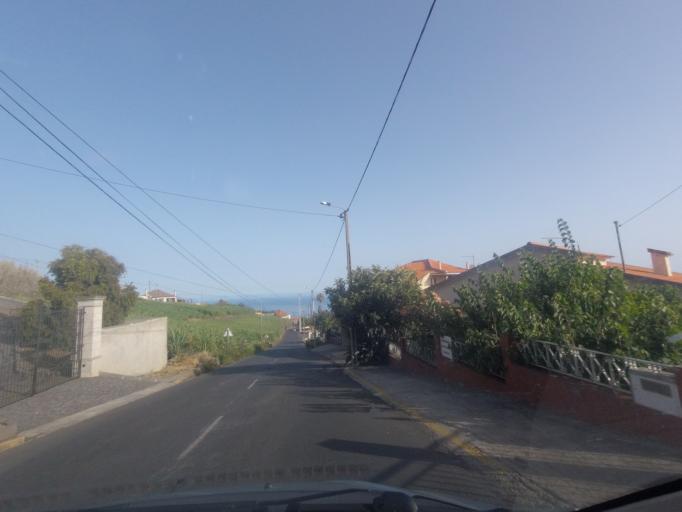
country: PT
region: Madeira
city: Ponta do Sol
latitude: 32.6933
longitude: -17.1112
